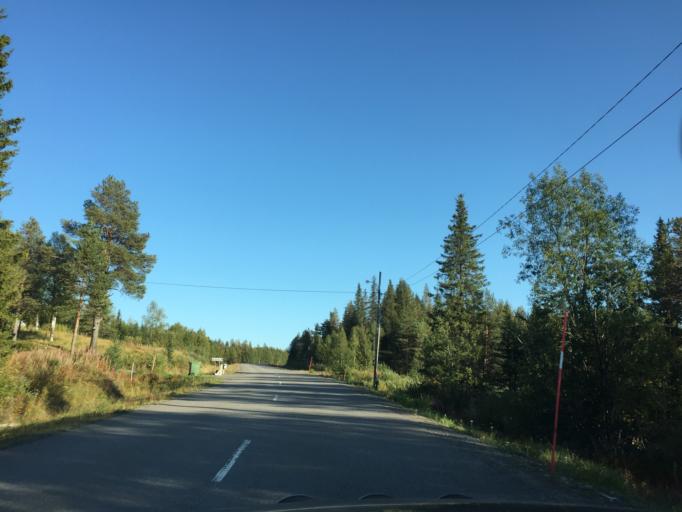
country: SE
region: Norrbotten
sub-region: Gallivare Kommun
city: Malmberget
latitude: 67.6397
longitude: 21.0643
